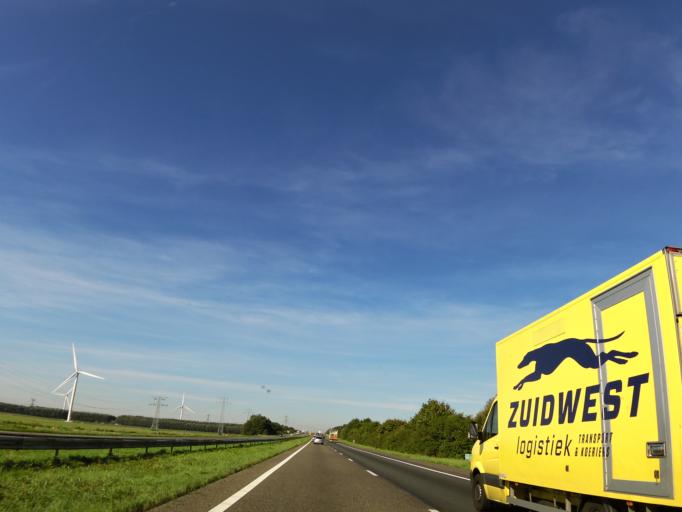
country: NL
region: North Brabant
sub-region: Gemeente Woensdrecht
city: Woensdrecht
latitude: 51.4291
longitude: 4.2502
